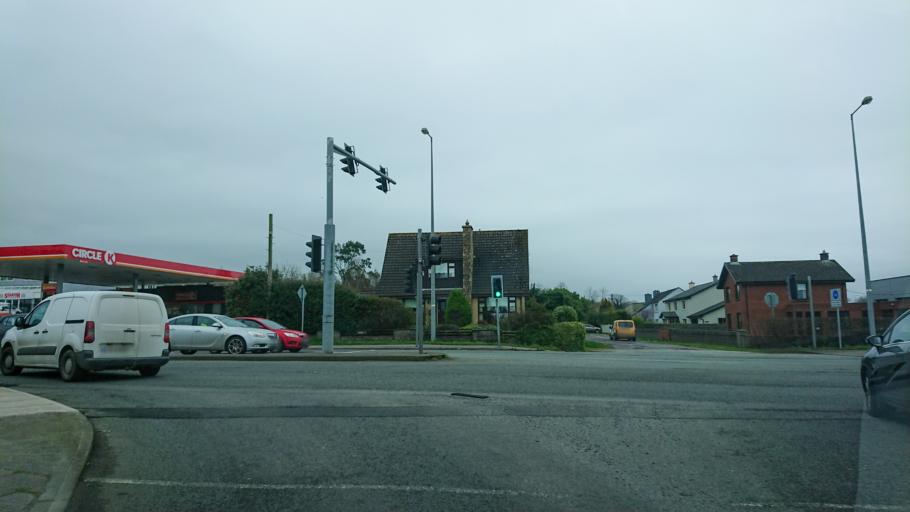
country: IE
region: Munster
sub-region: County Cork
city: Cork
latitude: 51.8732
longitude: -8.5230
